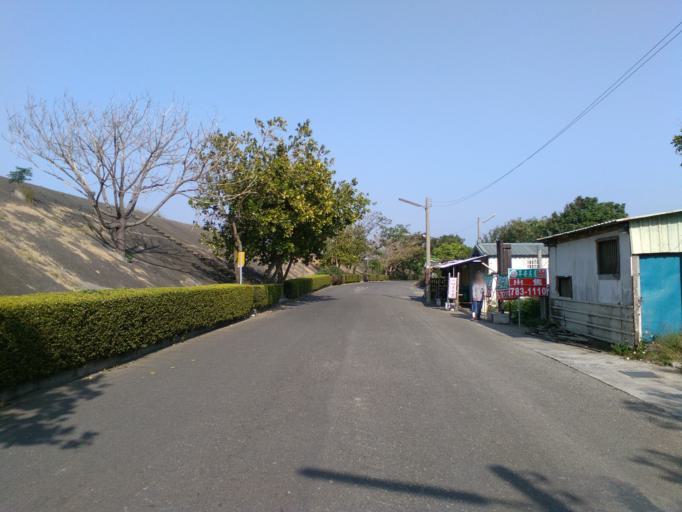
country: TW
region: Taiwan
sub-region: Chiayi
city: Taibao
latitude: 23.5707
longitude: 120.3141
